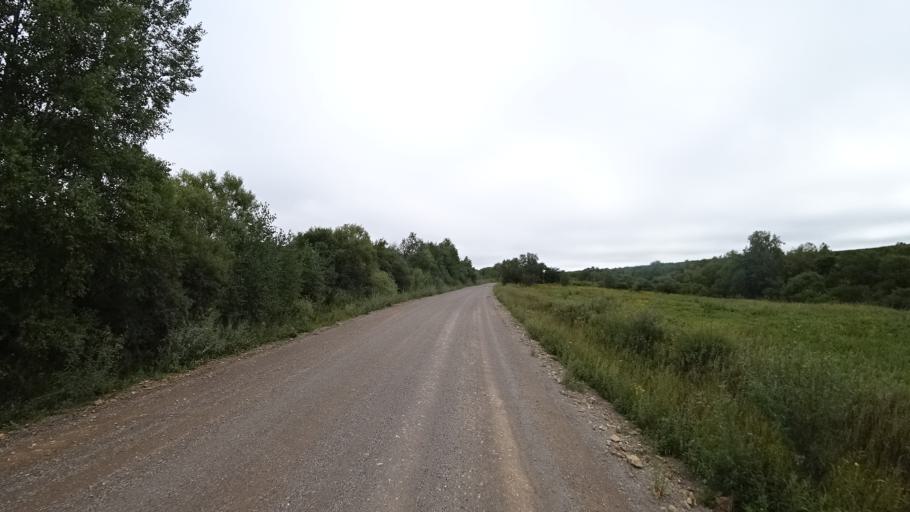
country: RU
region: Primorskiy
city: Ivanovka
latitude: 44.0475
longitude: 132.4909
